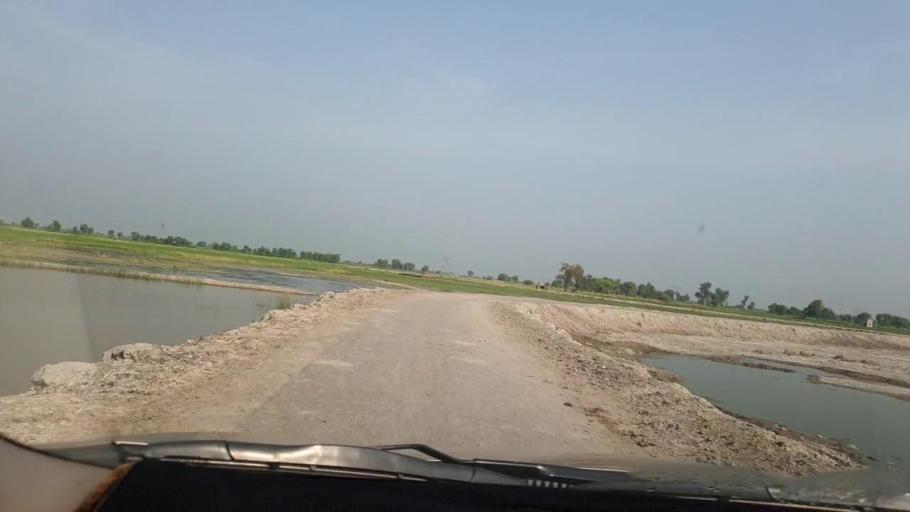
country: PK
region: Sindh
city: Goth Garelo
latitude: 27.4667
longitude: 68.0810
